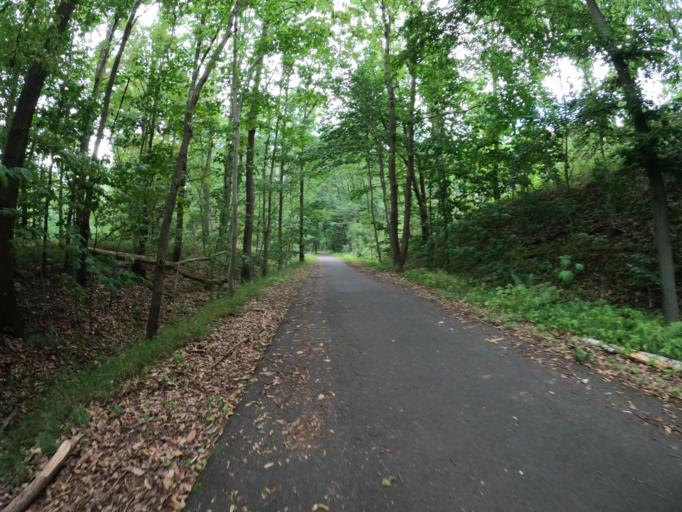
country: DE
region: Mecklenburg-Vorpommern
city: Woldegk
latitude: 53.3571
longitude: 13.5927
